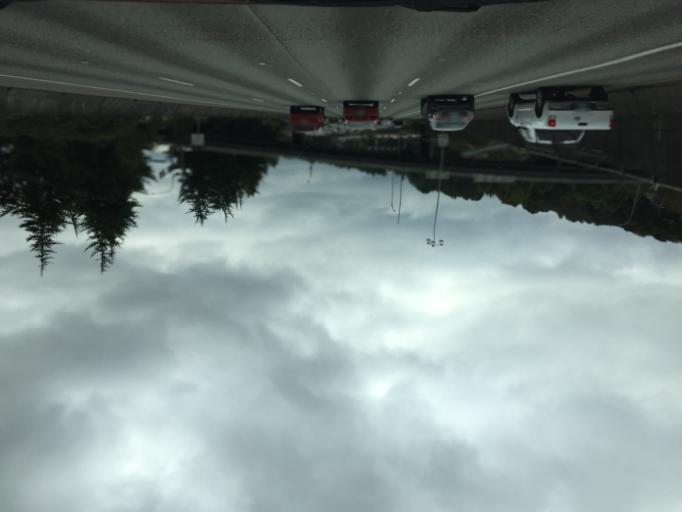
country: US
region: Washington
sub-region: King County
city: White Center
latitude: 47.5491
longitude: -122.3132
